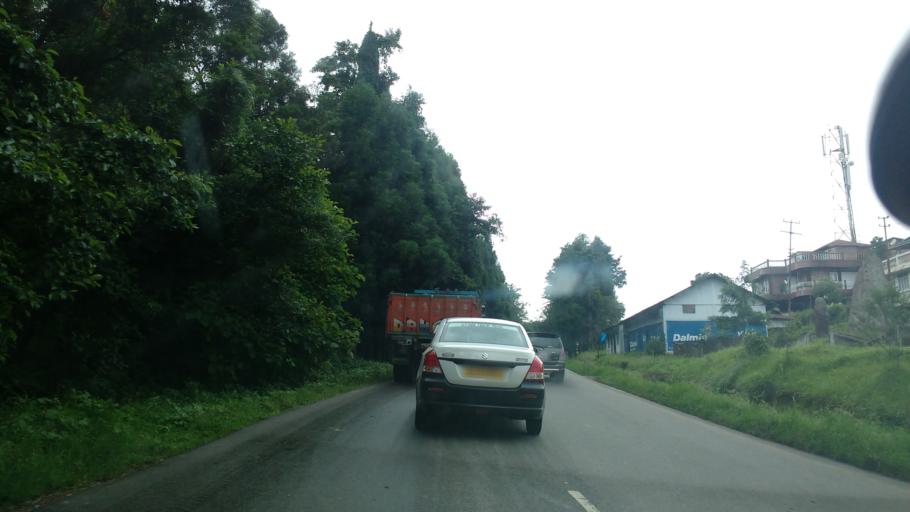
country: IN
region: Meghalaya
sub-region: East Khasi Hills
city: Shillong
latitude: 25.5519
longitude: 91.8437
